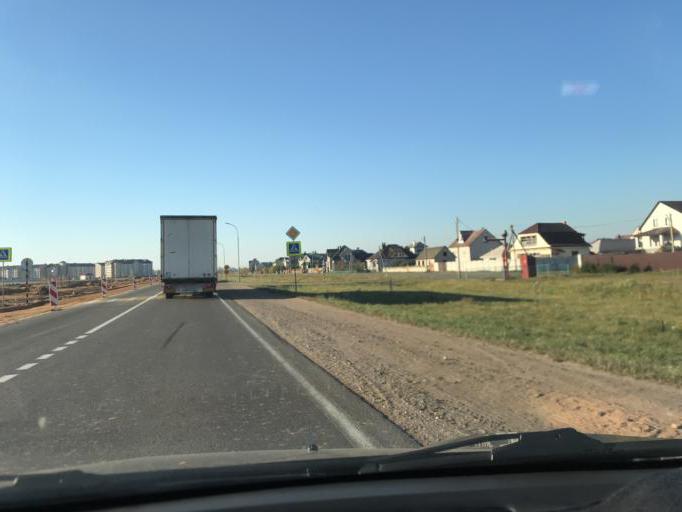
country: BY
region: Minsk
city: Slutsk
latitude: 53.0438
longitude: 27.5767
